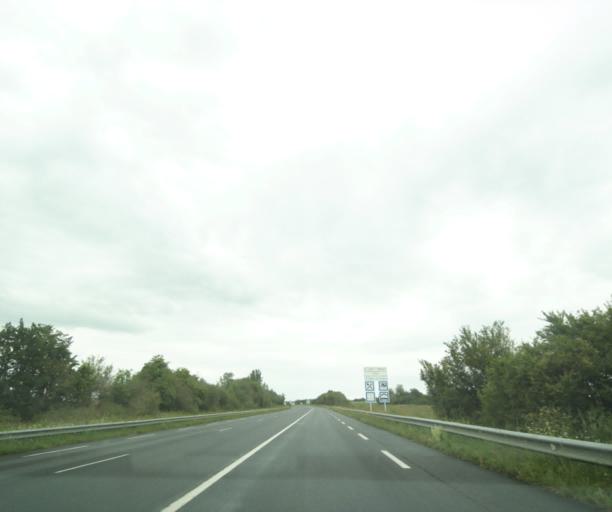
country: FR
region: Poitou-Charentes
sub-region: Departement des Deux-Sevres
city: Viennay
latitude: 46.7695
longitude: -0.2192
